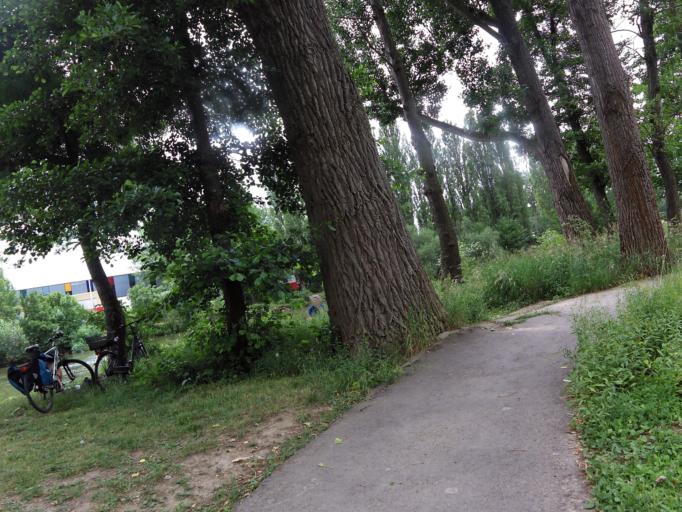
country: DE
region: Bavaria
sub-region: Regierungsbezirk Unterfranken
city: Wuerzburg
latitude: 49.7687
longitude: 9.9482
